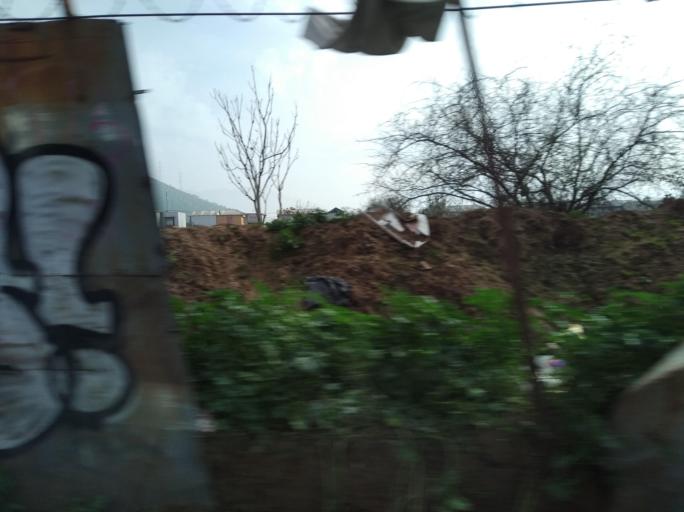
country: CL
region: Santiago Metropolitan
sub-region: Provincia de Chacabuco
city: Lampa
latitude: -33.2928
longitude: -70.8850
